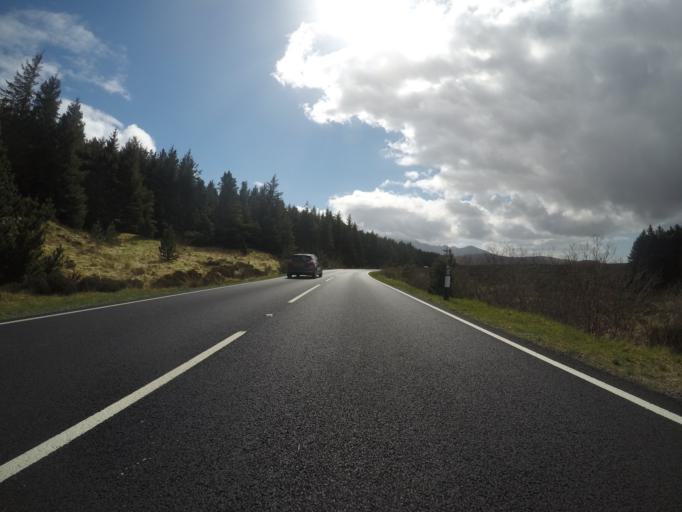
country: GB
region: Scotland
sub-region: Highland
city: Isle of Skye
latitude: 57.3283
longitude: -6.2029
